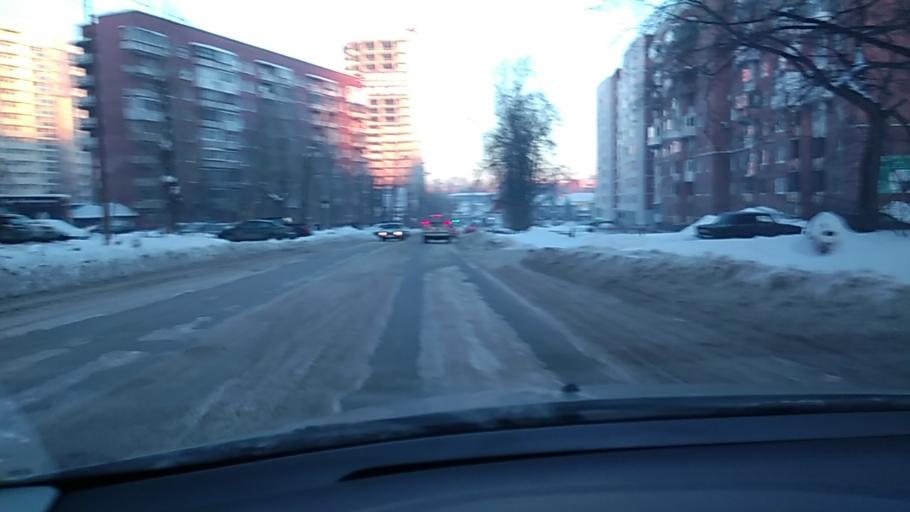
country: RU
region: Sverdlovsk
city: Yekaterinburg
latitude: 56.8619
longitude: 60.6237
